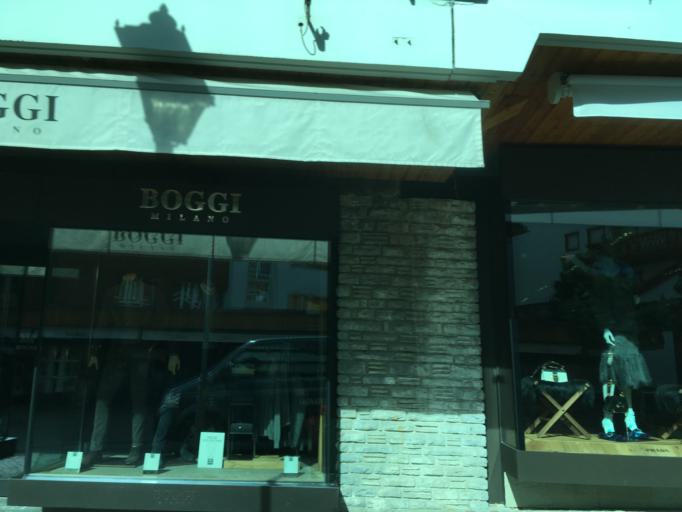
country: CH
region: Valais
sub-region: Sierre District
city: Montana
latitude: 46.3056
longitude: 7.4675
